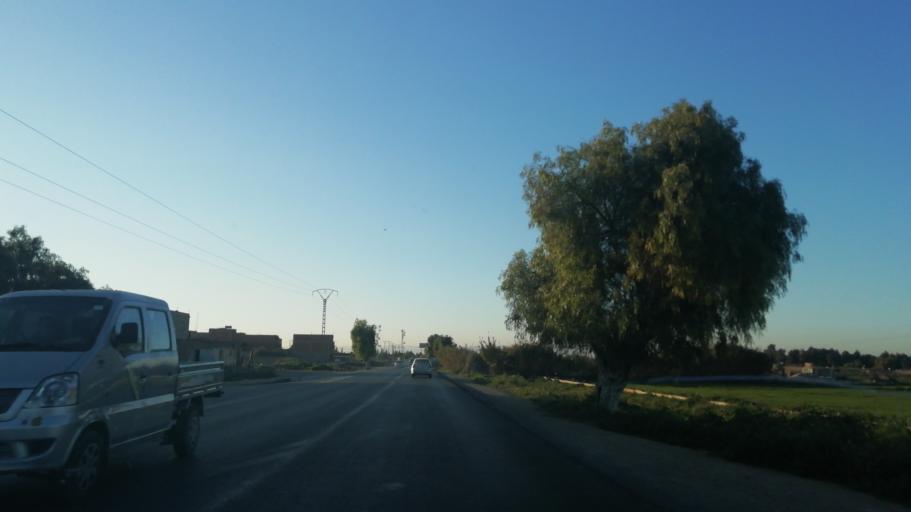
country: DZ
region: Relizane
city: Relizane
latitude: 35.7646
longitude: 0.6429
